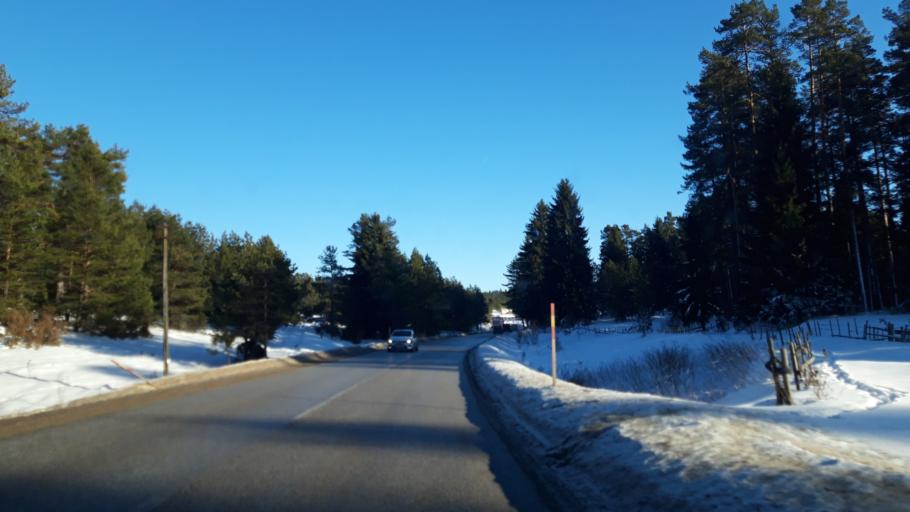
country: BA
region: Republika Srpska
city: Sokolac
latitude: 43.9191
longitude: 18.6929
